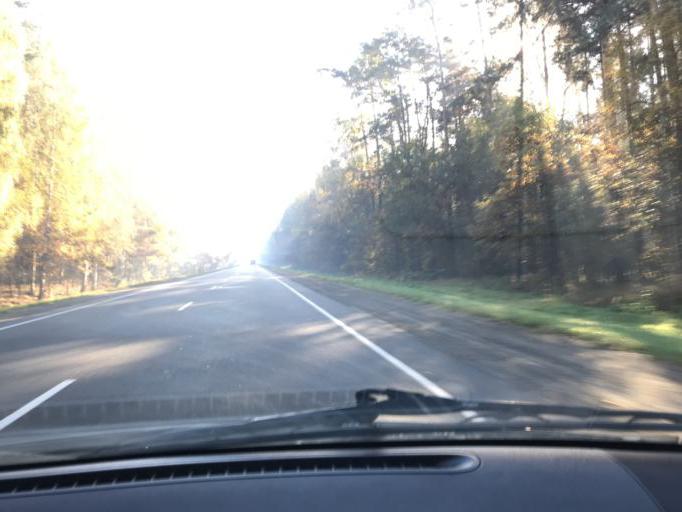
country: BY
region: Brest
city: Horad Luninyets
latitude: 52.2867
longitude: 26.7948
